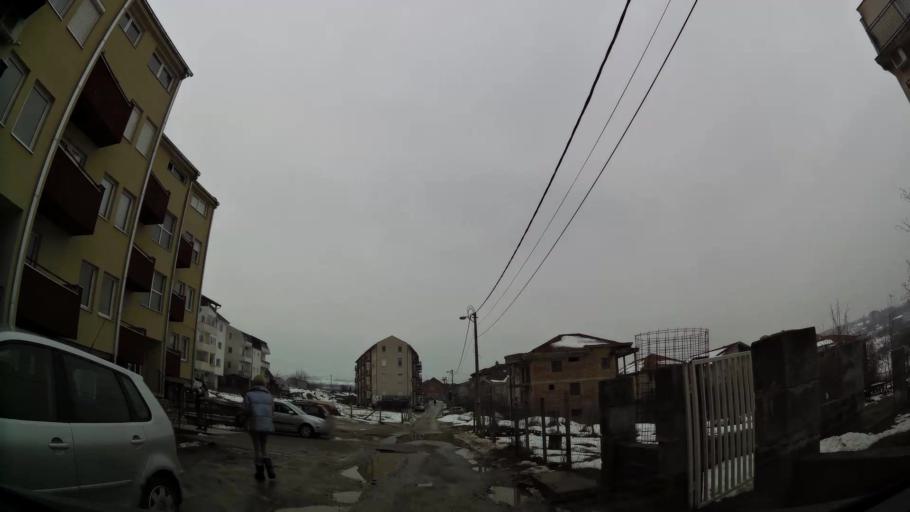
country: RS
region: Central Serbia
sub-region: Belgrade
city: Vozdovac
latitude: 44.7606
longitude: 20.5011
